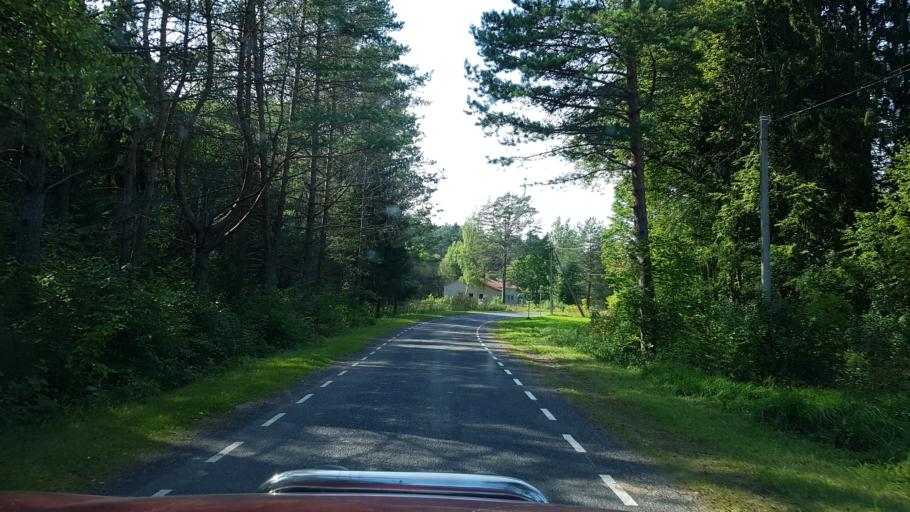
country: EE
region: Viljandimaa
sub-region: Suure-Jaani vald
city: Suure-Jaani
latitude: 58.3927
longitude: 25.3517
